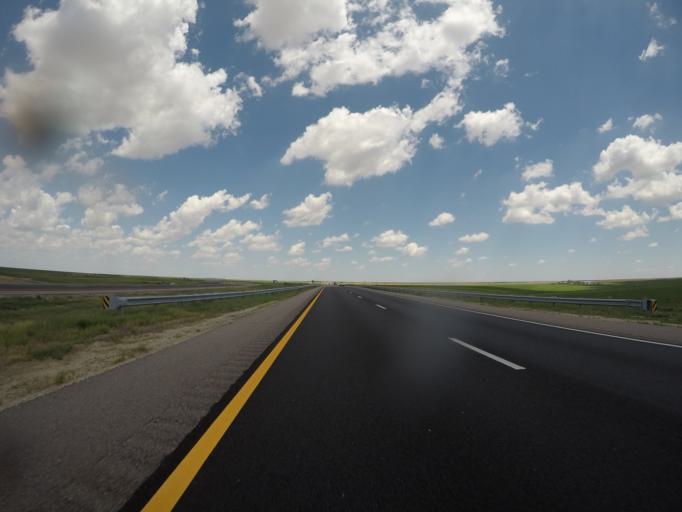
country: US
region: Kansas
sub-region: Sherman County
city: Goodland
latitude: 39.3300
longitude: -101.4856
